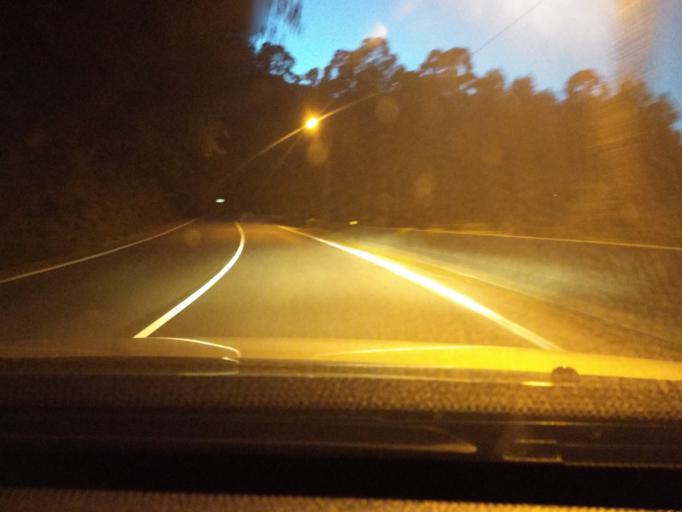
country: ES
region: Galicia
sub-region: Provincia de Pontevedra
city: Moana
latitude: 42.2986
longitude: -8.7416
